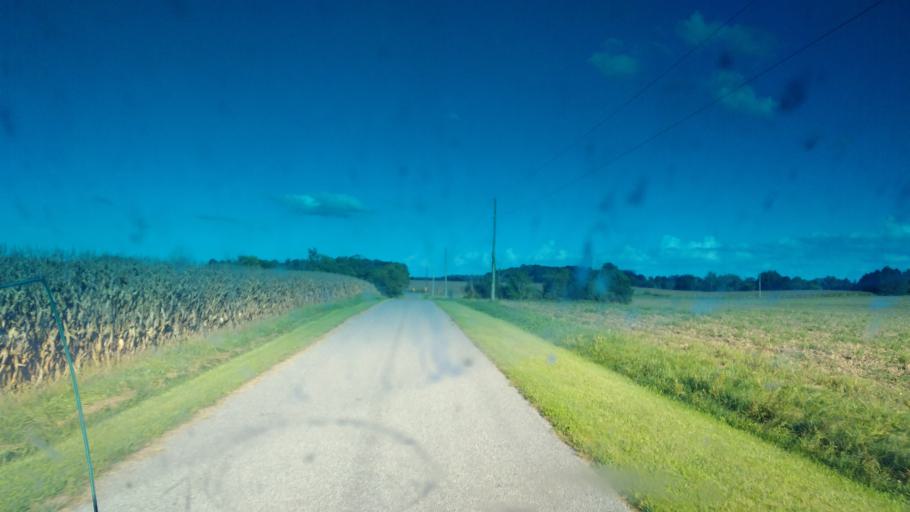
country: US
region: Ohio
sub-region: Wyandot County
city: Carey
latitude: 40.9375
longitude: -83.4896
